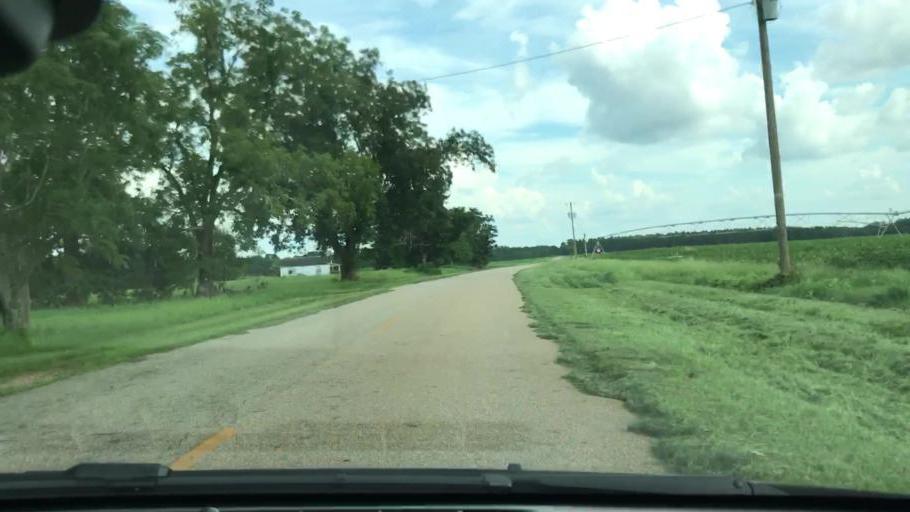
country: US
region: Georgia
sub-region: Clay County
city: Fort Gaines
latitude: 31.5666
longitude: -84.9892
